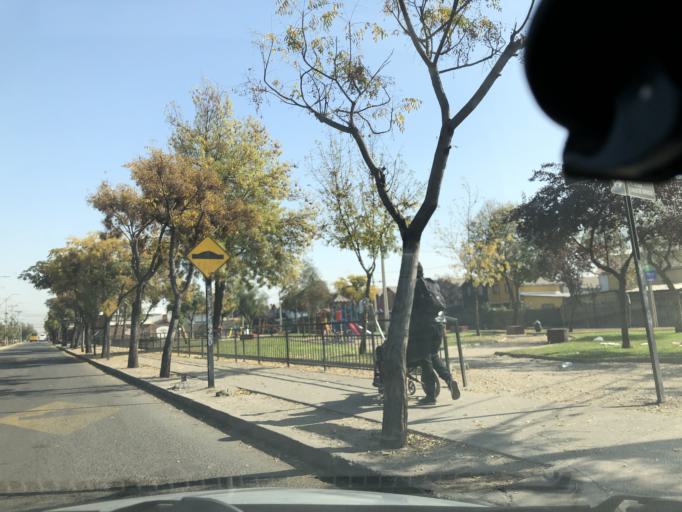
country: CL
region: Santiago Metropolitan
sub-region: Provincia de Cordillera
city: Puente Alto
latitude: -33.6036
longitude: -70.5552
